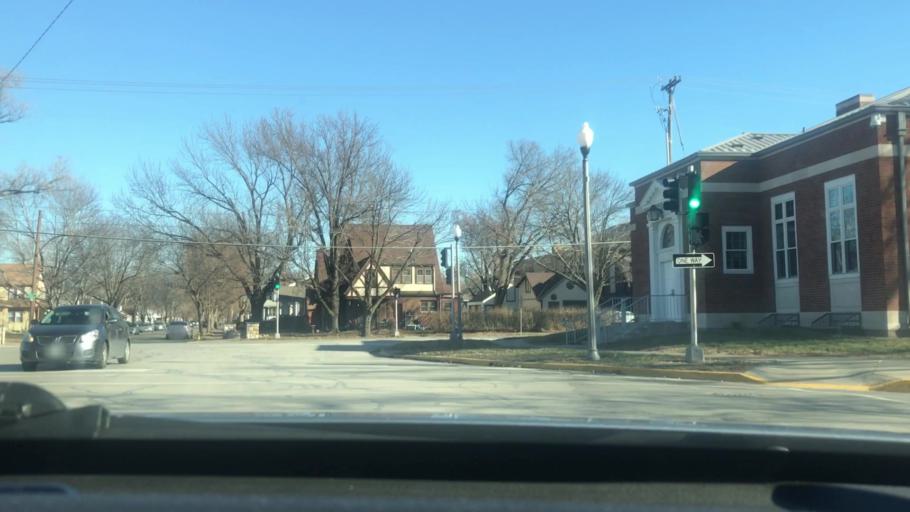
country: US
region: Missouri
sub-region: Clay County
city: North Kansas City
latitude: 39.1452
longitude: -94.5726
